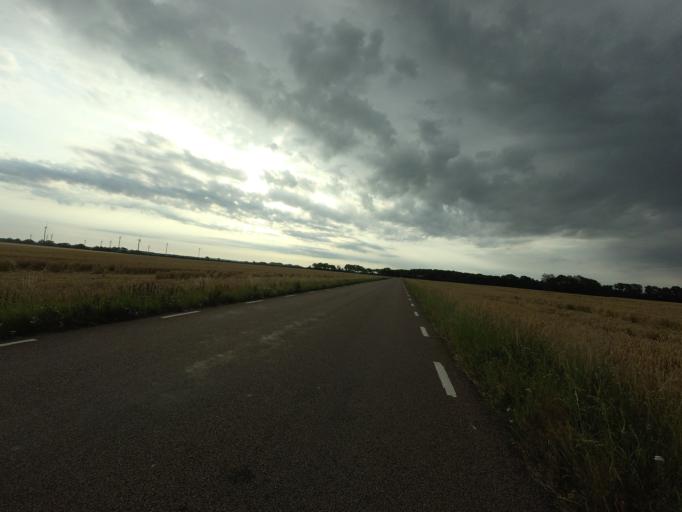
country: SE
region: Skane
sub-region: Helsingborg
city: Odakra
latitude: 56.1539
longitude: 12.7239
